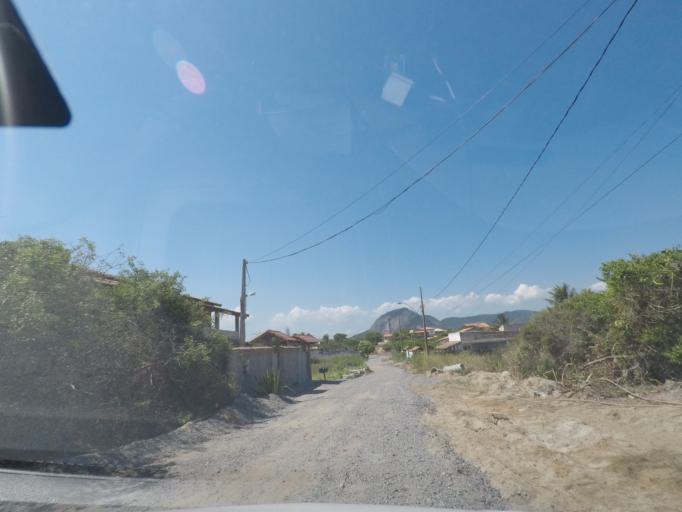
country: BR
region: Rio de Janeiro
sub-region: Marica
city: Marica
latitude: -22.9731
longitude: -42.9154
